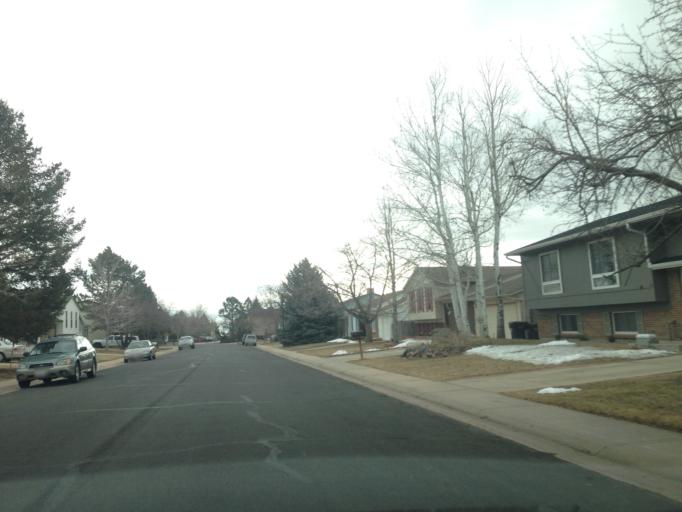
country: US
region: Colorado
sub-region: Boulder County
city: Louisville
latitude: 39.9836
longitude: -105.1589
